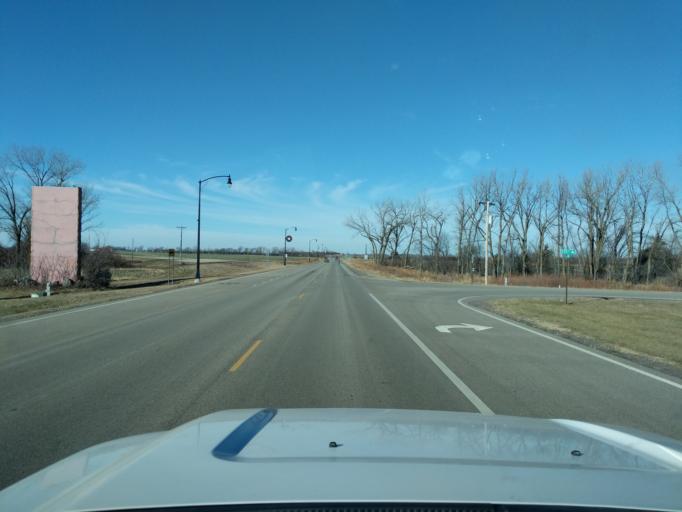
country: US
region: Minnesota
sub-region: Yellow Medicine County
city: Granite Falls
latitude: 44.7669
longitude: -95.5357
